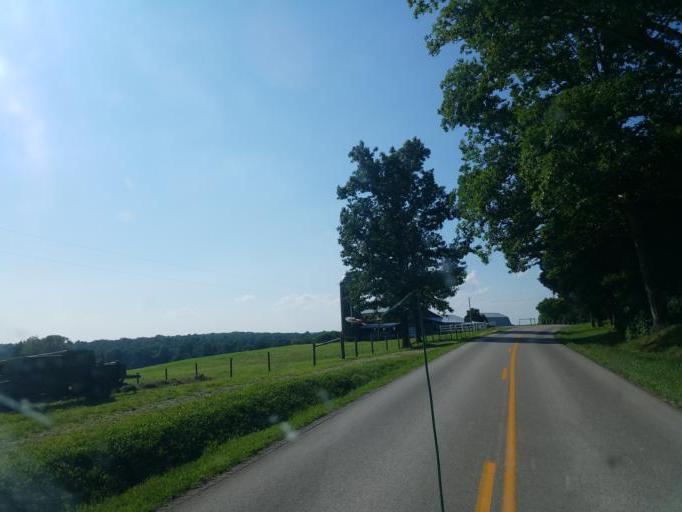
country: US
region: Kentucky
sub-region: Hart County
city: Munfordville
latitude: 37.3185
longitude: -86.0612
